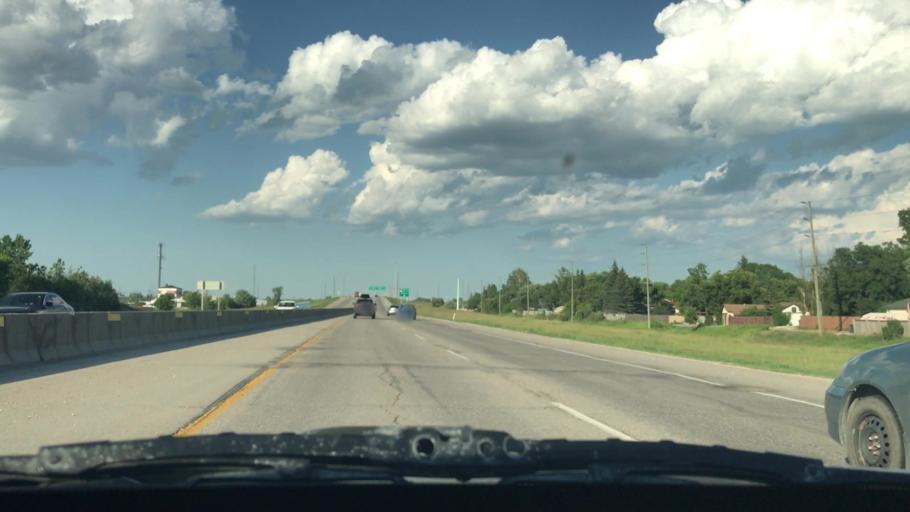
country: CA
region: Manitoba
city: Winnipeg
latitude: 49.7731
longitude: -97.1685
